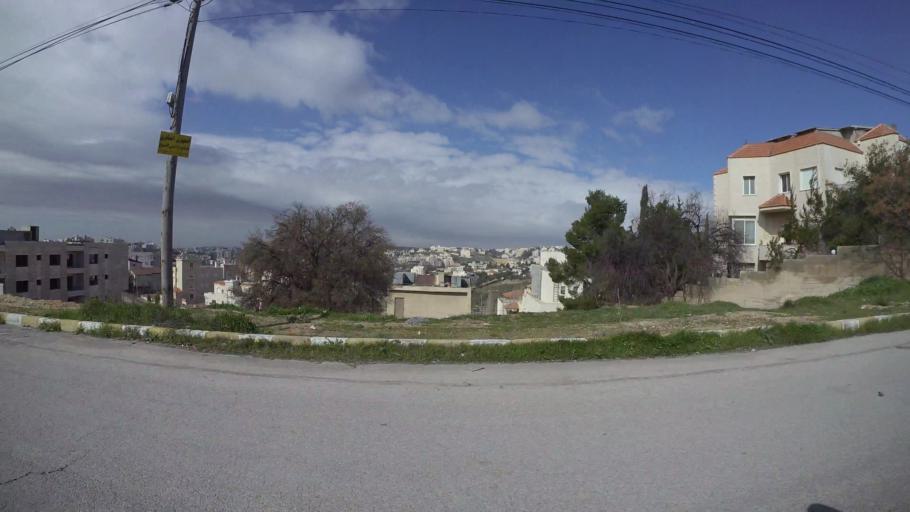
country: JO
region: Amman
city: Al Jubayhah
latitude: 32.0084
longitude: 35.8423
